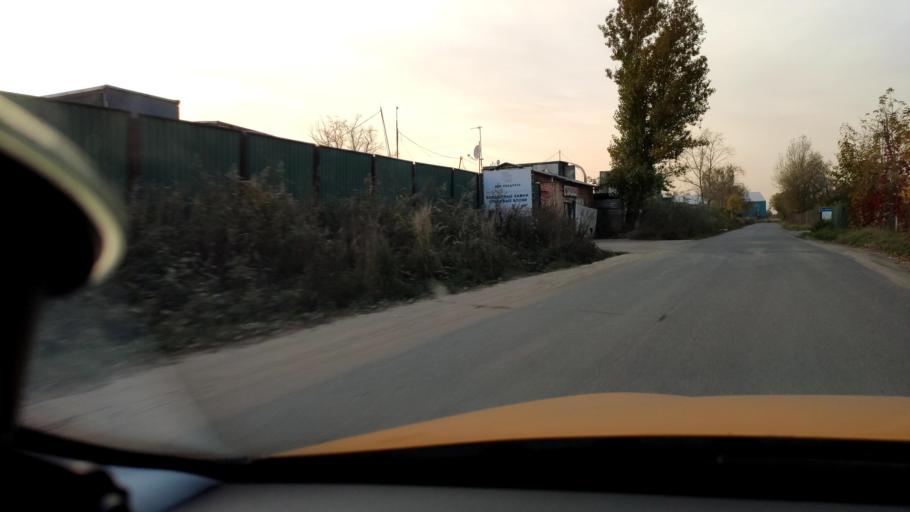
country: RU
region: Moskovskaya
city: Pirogovskiy
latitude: 55.9650
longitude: 37.6689
